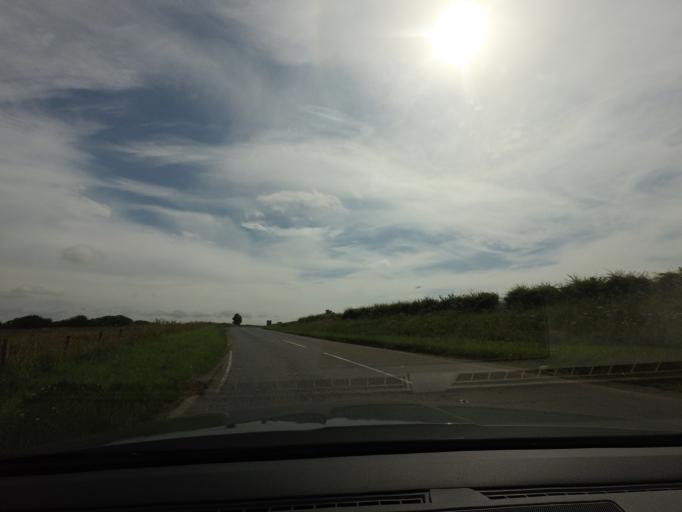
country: GB
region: Scotland
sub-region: Aberdeenshire
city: Rosehearty
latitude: 57.6033
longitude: -2.2192
